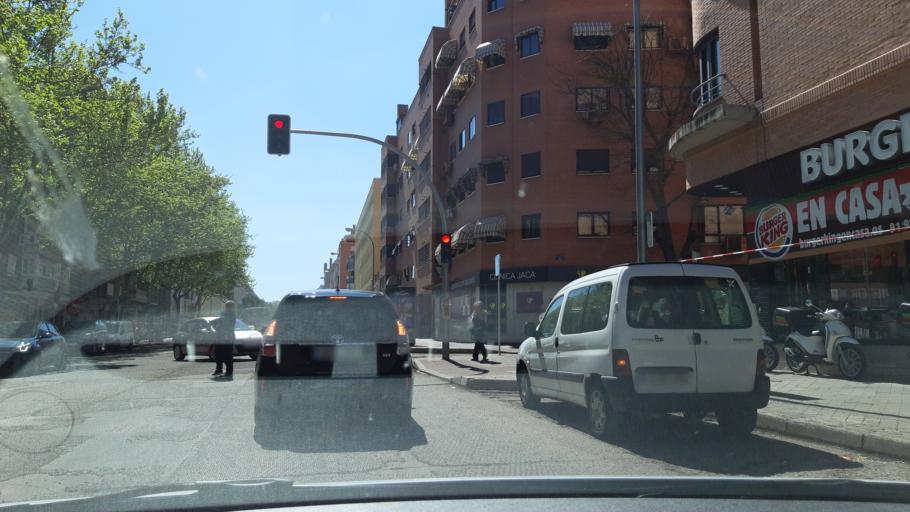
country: ES
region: Madrid
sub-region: Provincia de Madrid
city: San Blas
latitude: 40.4480
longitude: -3.6102
